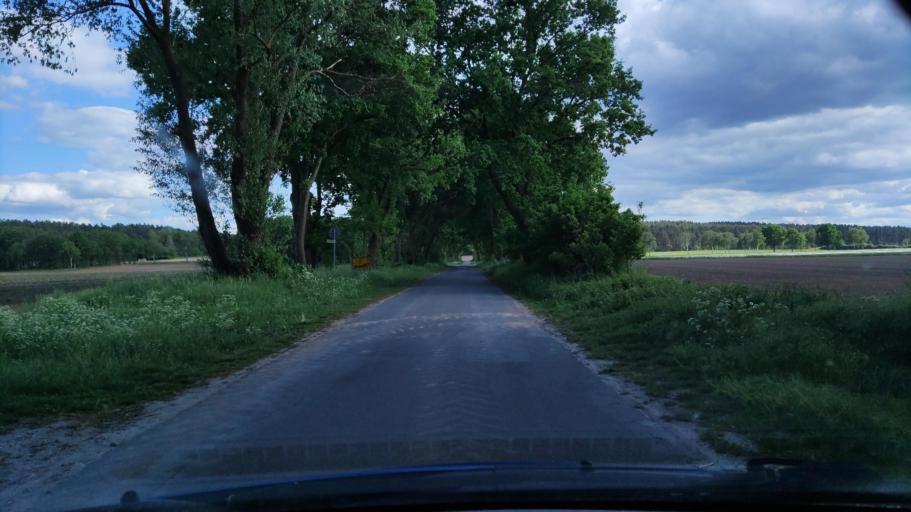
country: DE
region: Lower Saxony
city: Hitzacker
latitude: 53.1472
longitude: 10.9864
